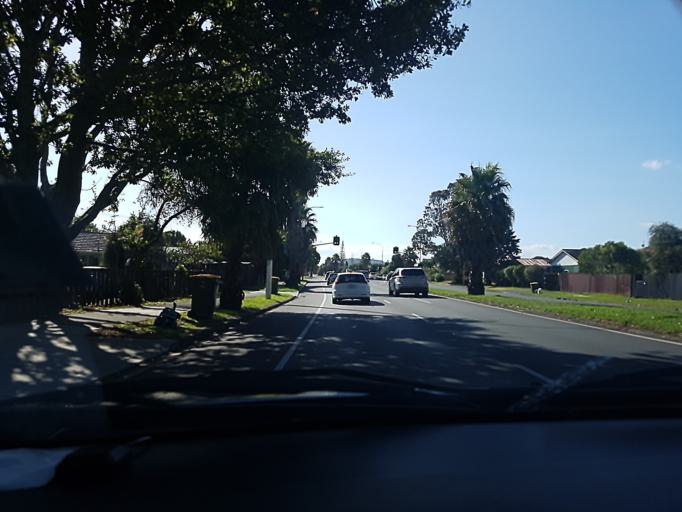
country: NZ
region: Auckland
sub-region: Auckland
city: Tamaki
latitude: -36.9211
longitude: 174.8780
